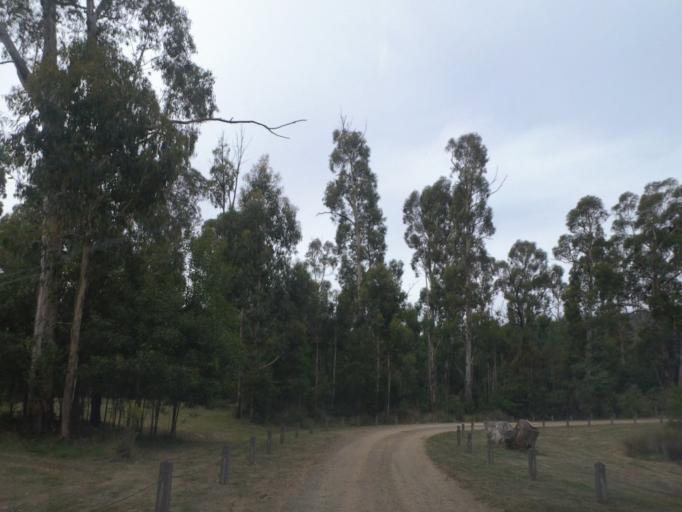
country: AU
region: Victoria
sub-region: Murrindindi
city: Alexandra
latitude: -37.3887
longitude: 145.5531
